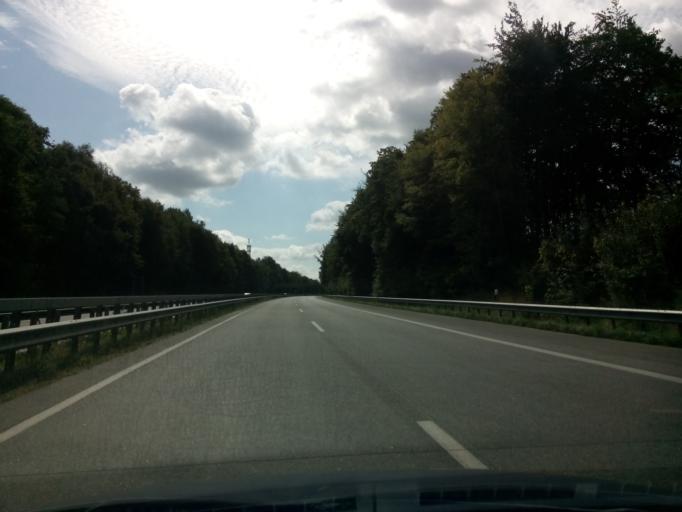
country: DE
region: Lower Saxony
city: Ritterhude
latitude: 53.1955
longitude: 8.6938
